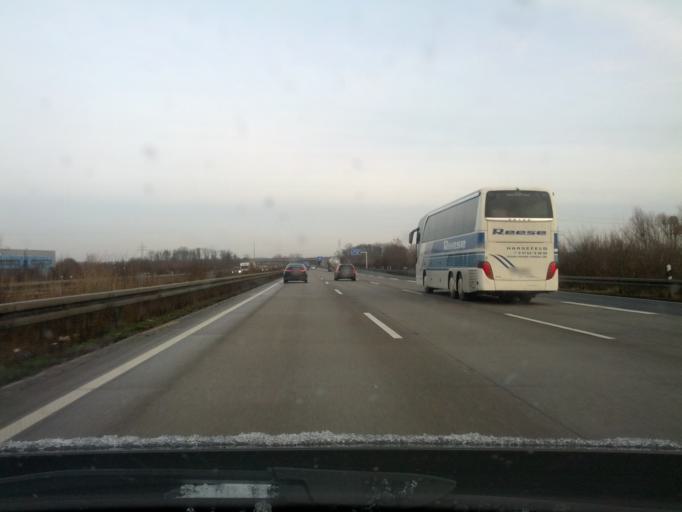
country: DE
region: Lower Saxony
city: Laatzen
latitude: 52.3545
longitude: 9.8799
